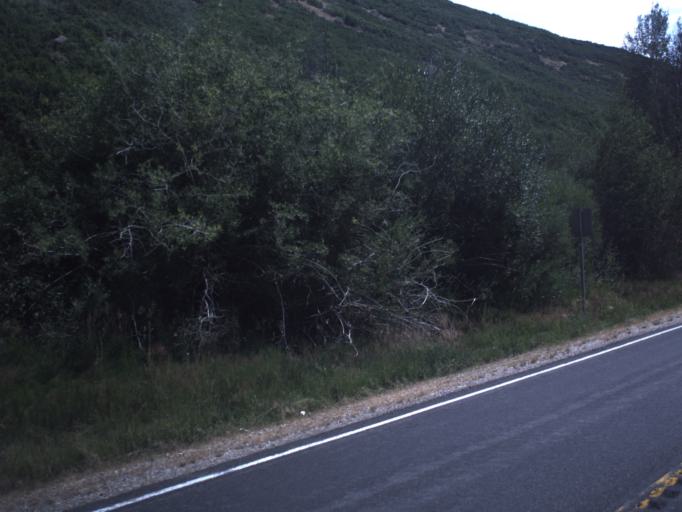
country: US
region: Utah
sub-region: Summit County
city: Francis
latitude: 40.5728
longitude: -111.2069
